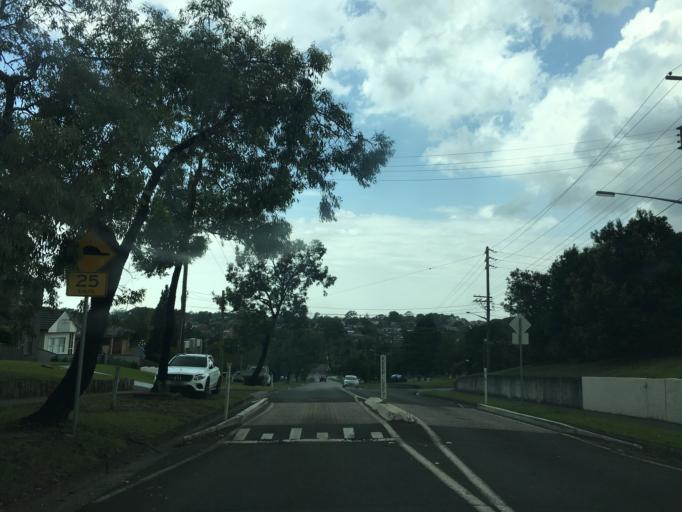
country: AU
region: New South Wales
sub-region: Ryde
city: Marsfield
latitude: -33.7922
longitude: 151.1075
